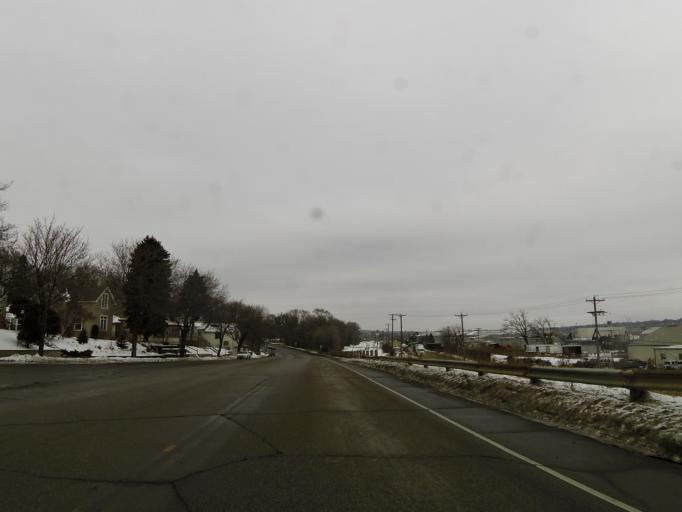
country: US
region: Minnesota
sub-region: Ramsey County
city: Saint Paul
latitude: 44.9234
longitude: -93.0633
